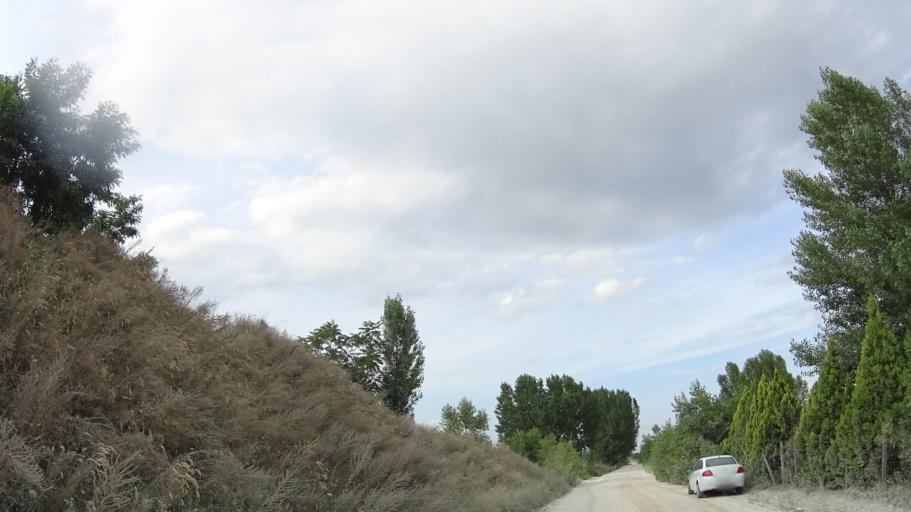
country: HU
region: Pest
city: Delegyhaza
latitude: 47.2581
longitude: 19.1062
